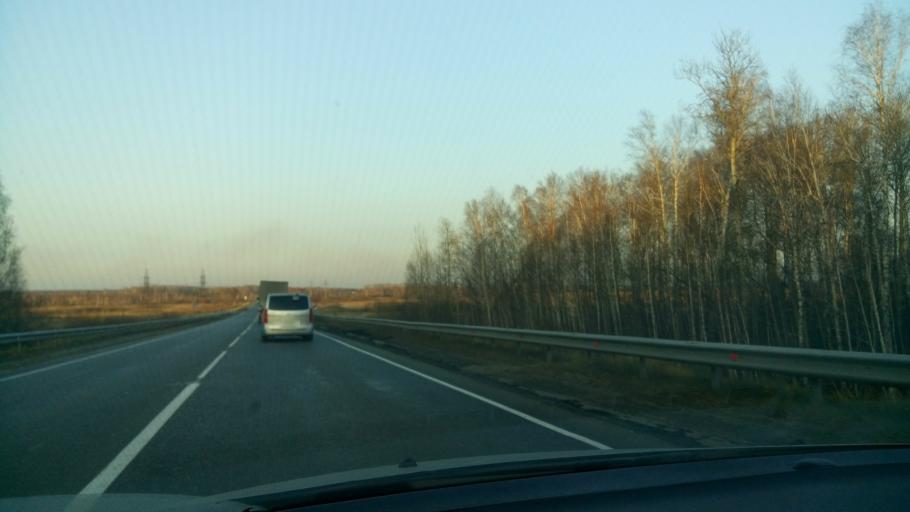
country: RU
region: Sverdlovsk
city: Yelanskiy
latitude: 56.7989
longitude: 62.5168
